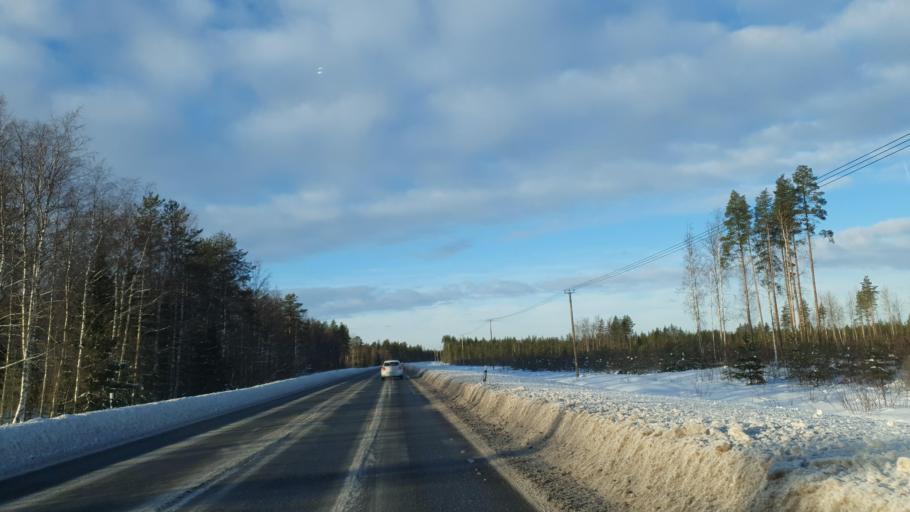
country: FI
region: Northern Ostrobothnia
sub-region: Oulu
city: Muhos
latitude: 64.7858
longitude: 26.2187
